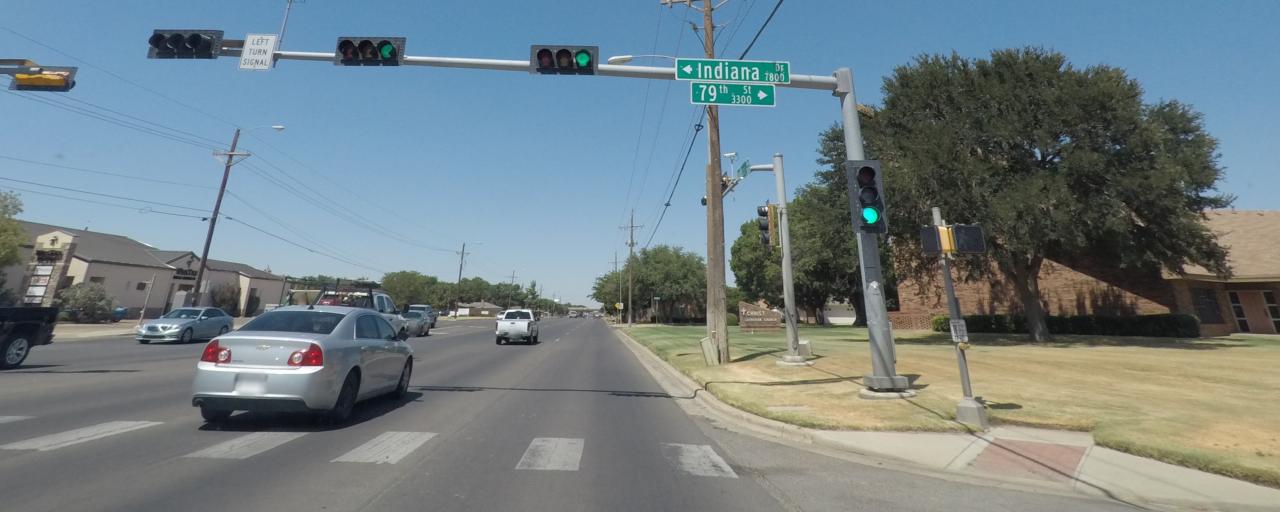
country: US
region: Texas
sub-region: Lubbock County
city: Lubbock
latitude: 33.5226
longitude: -101.8876
